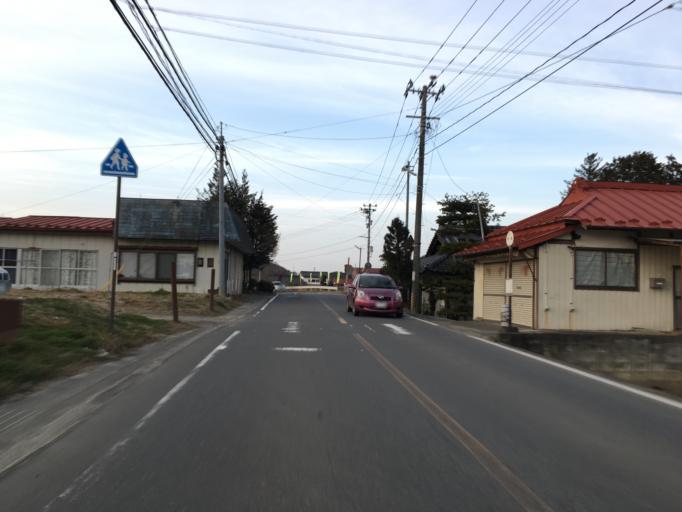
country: JP
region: Ibaraki
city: Daigo
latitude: 36.9333
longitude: 140.4085
